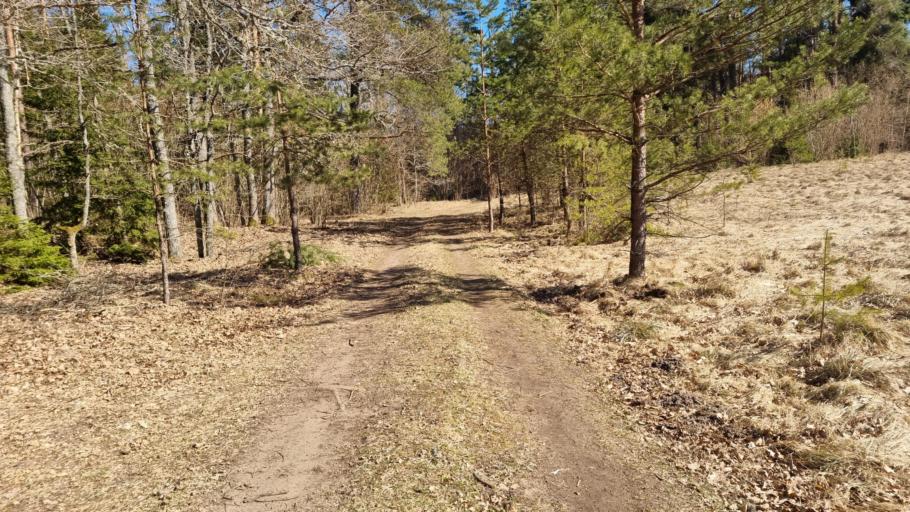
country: LV
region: Talsu Rajons
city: Stende
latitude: 57.0749
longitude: 22.4611
